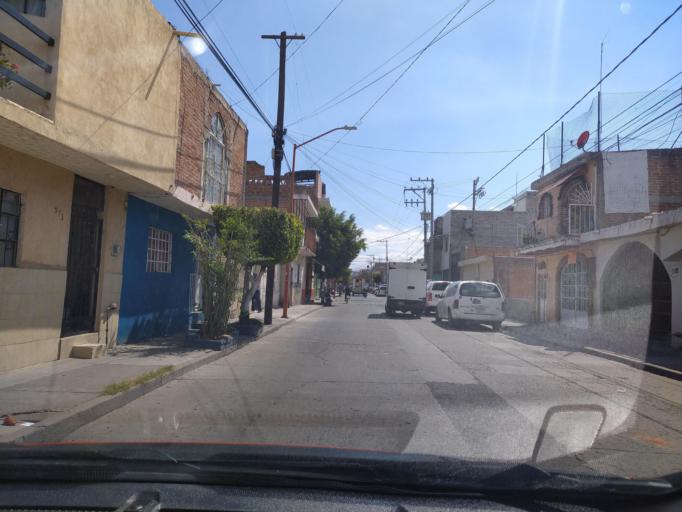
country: MX
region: Guanajuato
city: San Francisco del Rincon
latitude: 21.0143
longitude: -101.8529
